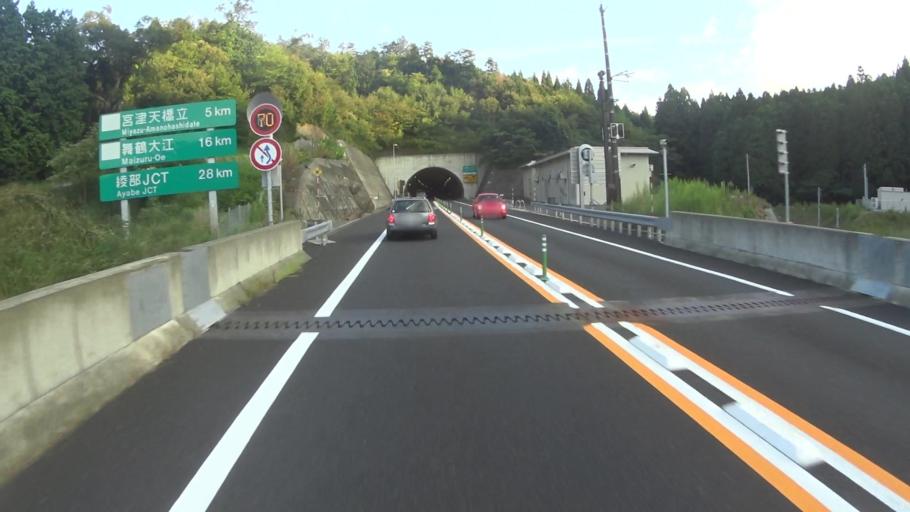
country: JP
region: Kyoto
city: Miyazu
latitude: 35.5422
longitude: 135.1559
